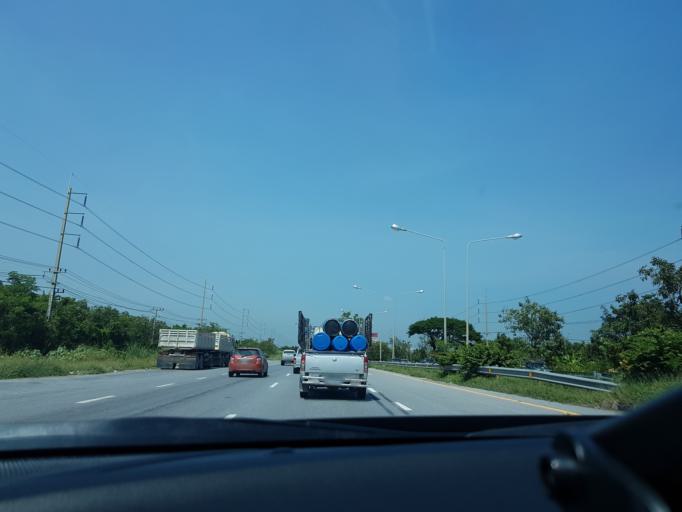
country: TH
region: Sara Buri
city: Saraburi
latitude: 14.5107
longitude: 100.9037
